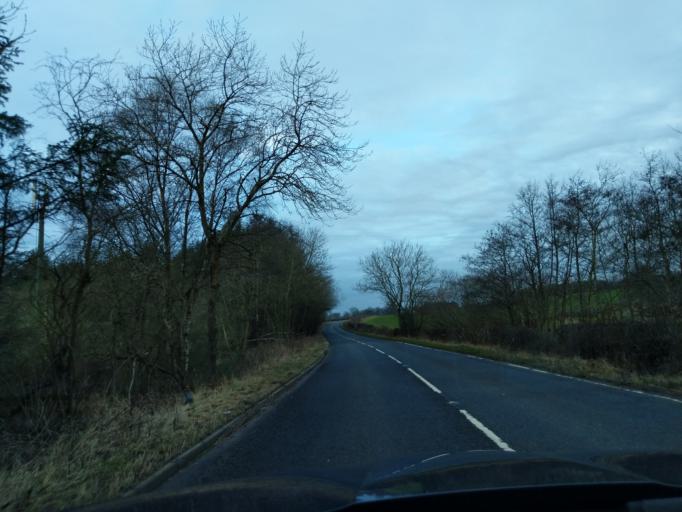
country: GB
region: England
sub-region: Northumberland
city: Rothley
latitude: 55.1227
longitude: -1.9179
